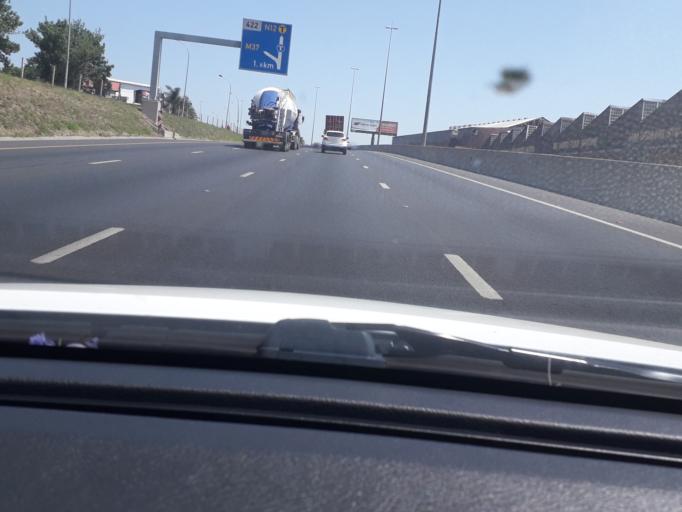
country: ZA
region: Gauteng
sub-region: Ekurhuleni Metropolitan Municipality
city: Germiston
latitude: -26.1694
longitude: 28.1913
